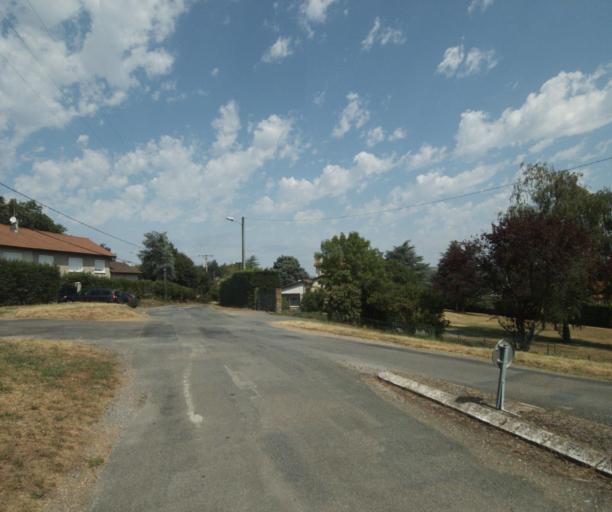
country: FR
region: Rhone-Alpes
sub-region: Departement du Rhone
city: Lentilly
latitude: 45.8432
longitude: 4.6600
